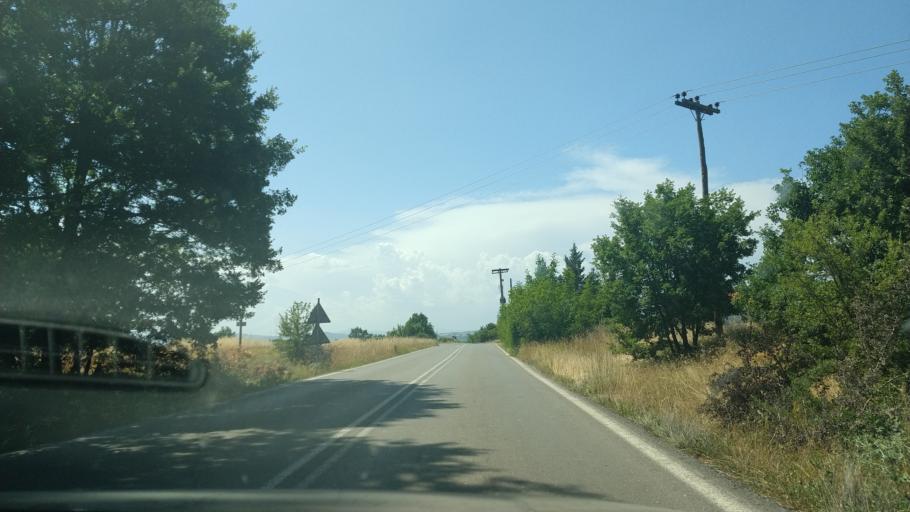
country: GR
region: West Macedonia
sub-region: Nomos Grevenon
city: Grevena
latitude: 40.0678
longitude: 21.4605
